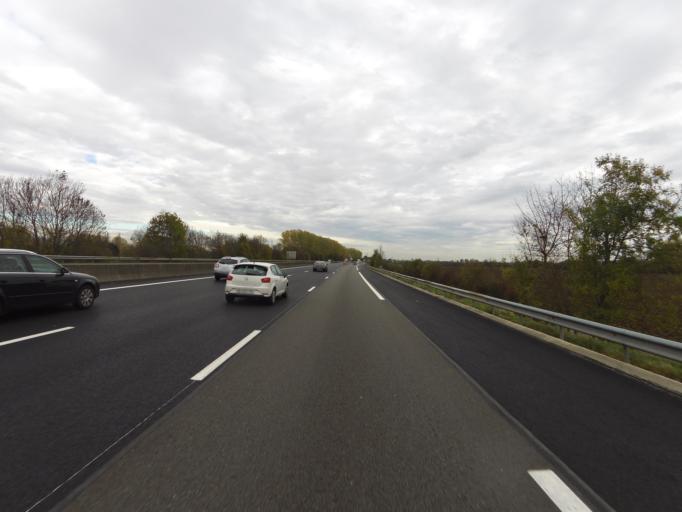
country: FR
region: Rhone-Alpes
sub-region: Departement du Rhone
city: Belleville
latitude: 46.0905
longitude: 4.7443
